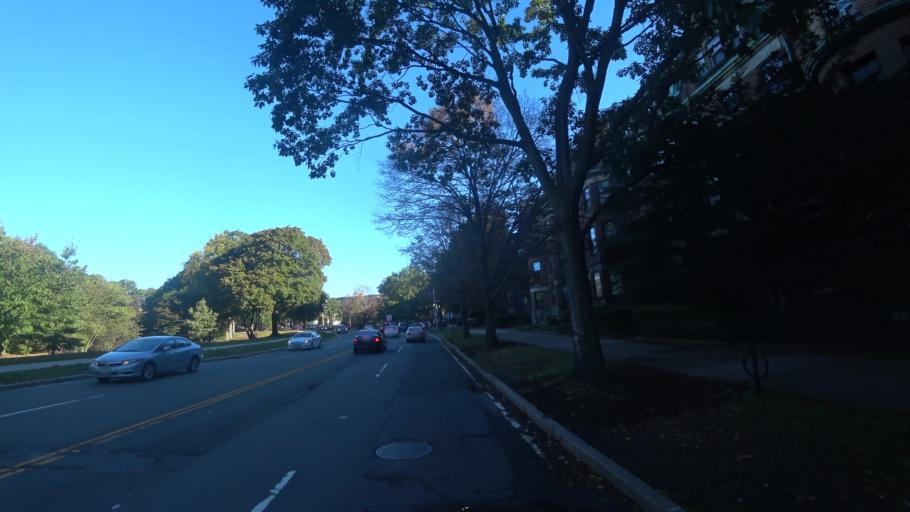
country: US
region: Massachusetts
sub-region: Norfolk County
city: Brookline
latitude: 42.3448
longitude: -71.0907
